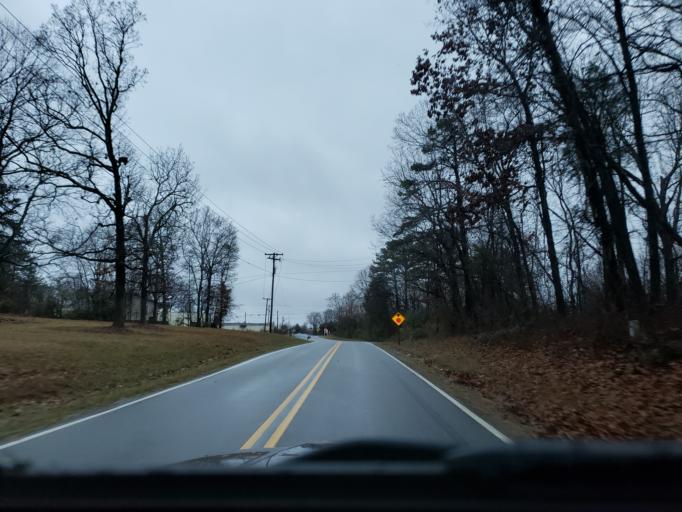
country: US
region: North Carolina
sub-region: Cleveland County
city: White Plains
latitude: 35.2001
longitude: -81.3888
